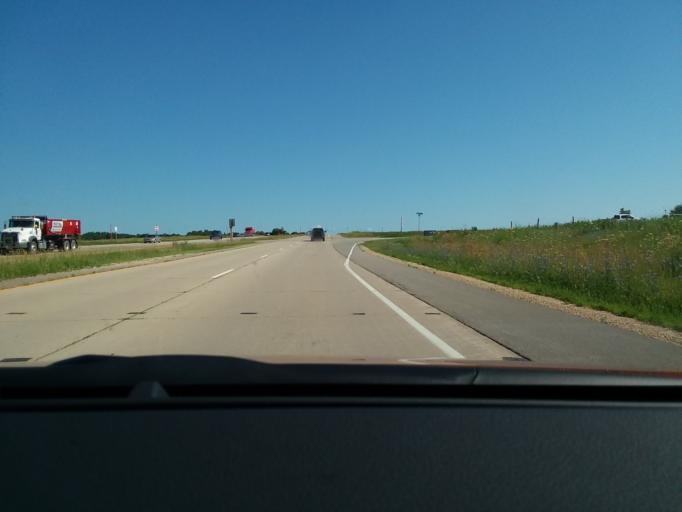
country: US
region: Wisconsin
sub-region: Dane County
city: Maple Bluff
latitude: 43.1529
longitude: -89.3247
